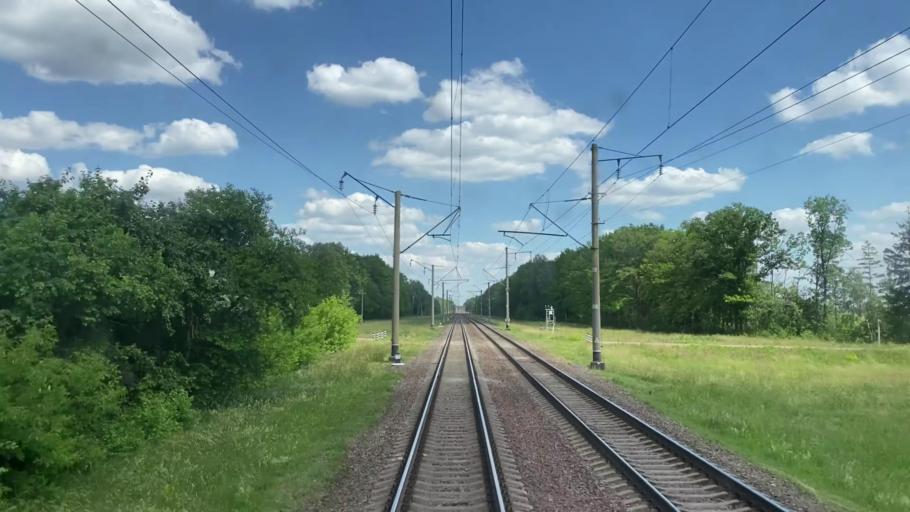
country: BY
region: Brest
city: Pruzhany
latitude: 52.4878
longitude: 24.5786
